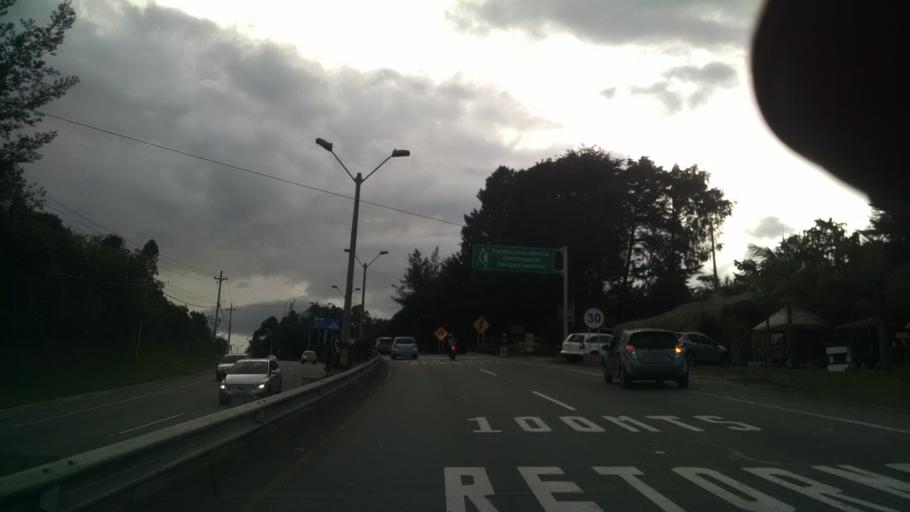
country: CO
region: Antioquia
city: Envigado
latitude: 6.1543
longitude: -75.5372
